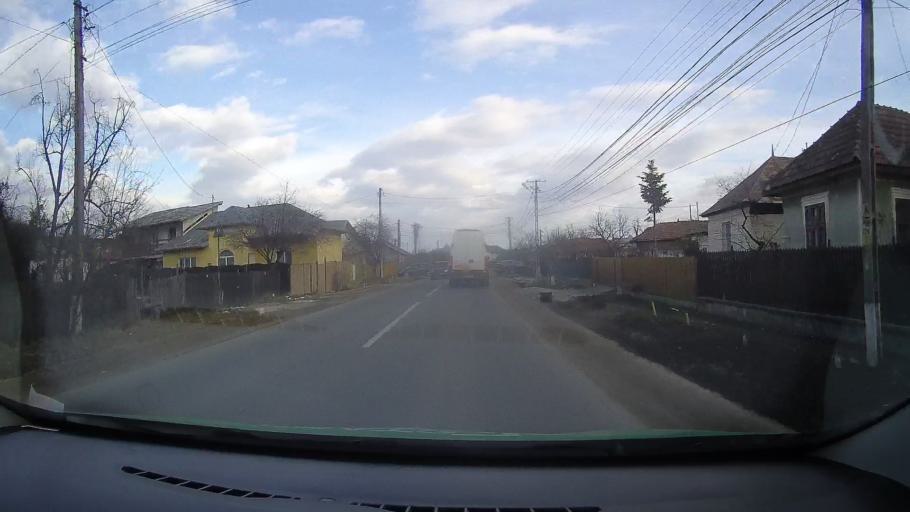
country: RO
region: Dambovita
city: Razvad
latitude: 44.9333
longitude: 25.5431
